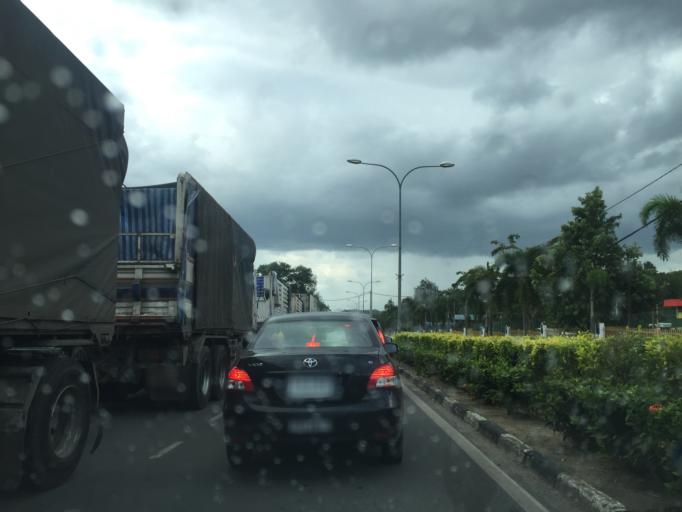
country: TH
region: Songkhla
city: Sadao
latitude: 6.5168
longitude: 100.4195
